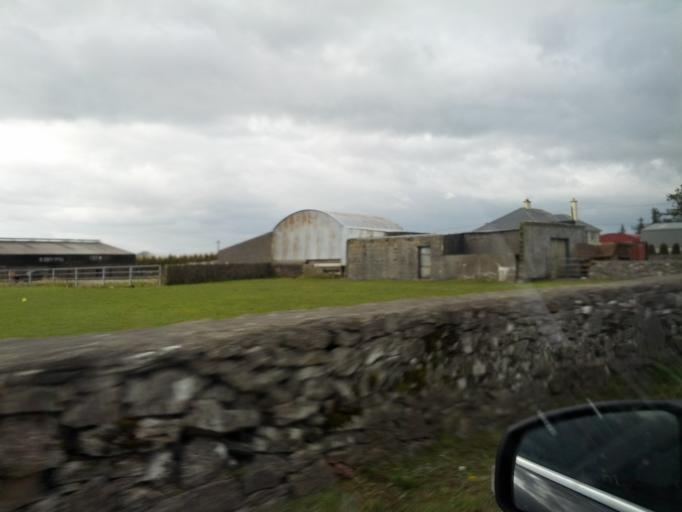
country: IE
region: Connaught
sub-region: County Galway
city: Athenry
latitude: 53.4463
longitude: -8.6345
